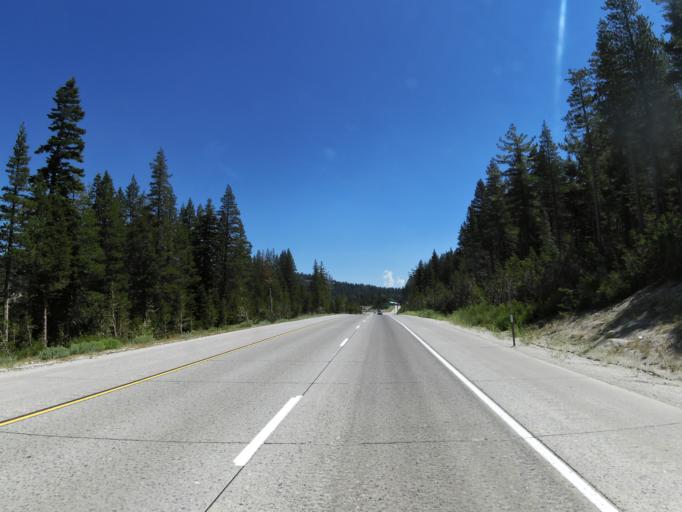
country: US
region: California
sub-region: Nevada County
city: Truckee
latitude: 39.3231
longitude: -120.3997
